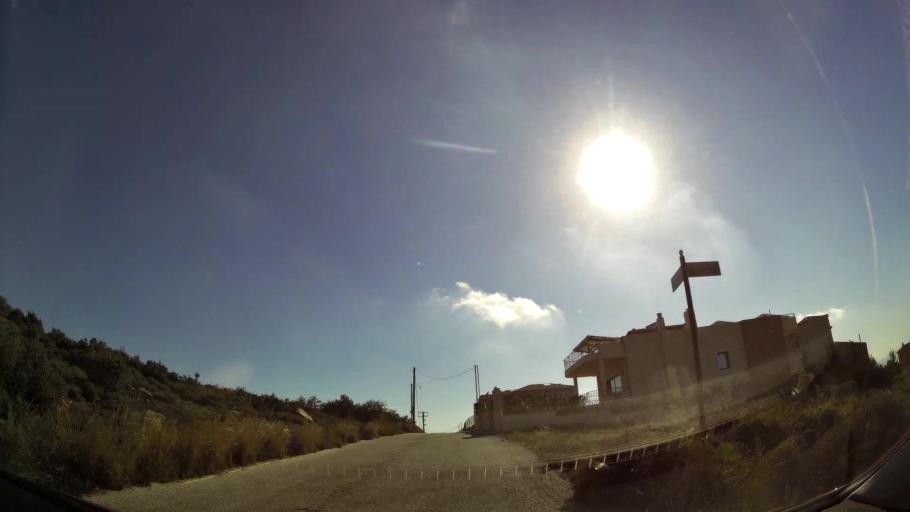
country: GR
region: Attica
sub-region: Nomarchia Anatolikis Attikis
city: Dioni
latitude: 38.0390
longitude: 23.9245
